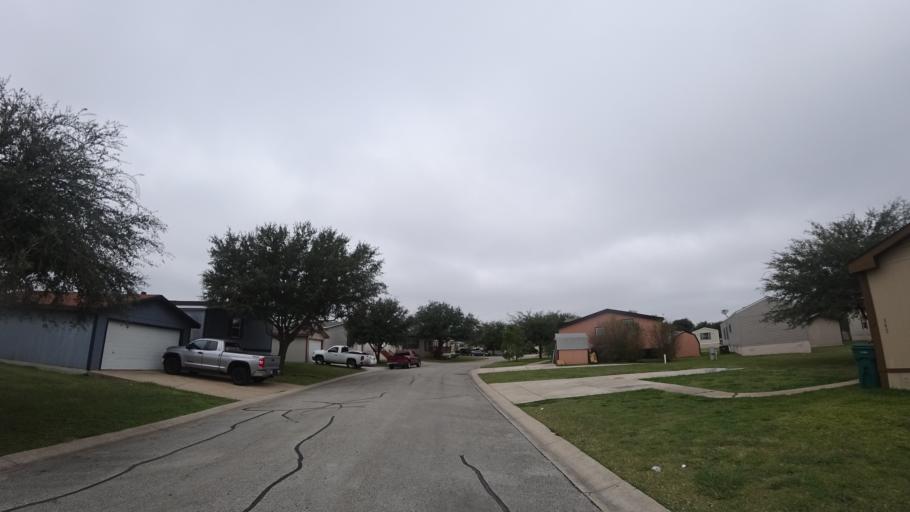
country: US
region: Texas
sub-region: Travis County
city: Pflugerville
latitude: 30.4157
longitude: -97.6054
